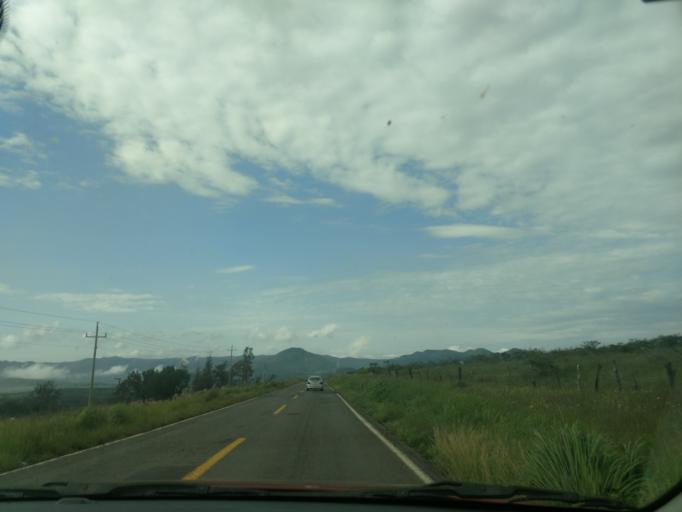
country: MX
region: Jalisco
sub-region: Atengo
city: Soyatlan del Oro
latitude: 20.5431
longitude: -104.3085
